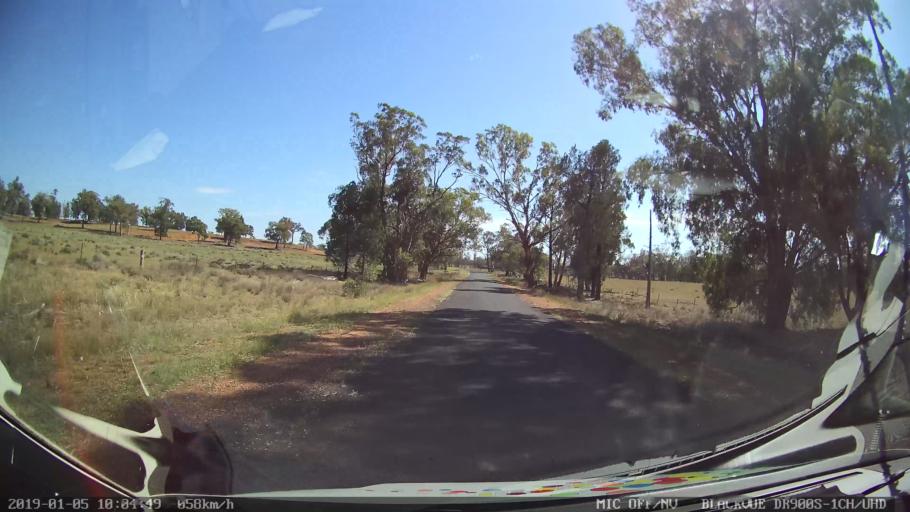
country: AU
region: New South Wales
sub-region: Gilgandra
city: Gilgandra
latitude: -31.6717
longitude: 148.8620
